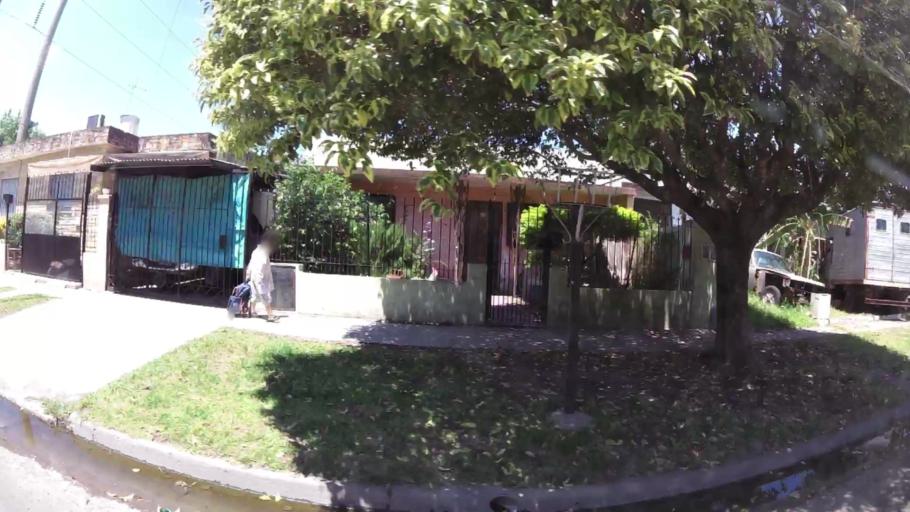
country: AR
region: Buenos Aires
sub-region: Partido de Merlo
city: Merlo
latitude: -34.6590
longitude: -58.6947
